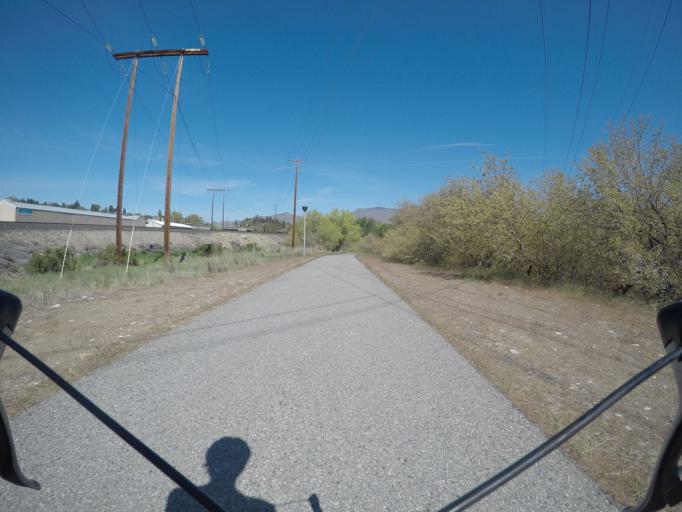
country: US
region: Washington
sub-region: Chelan County
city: Sunnyslope
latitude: 47.4553
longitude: -120.3332
